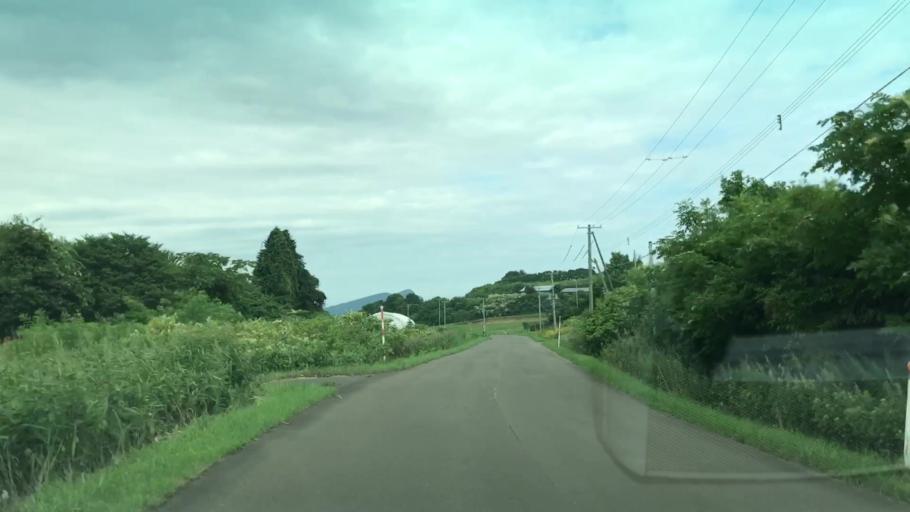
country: JP
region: Hokkaido
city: Yoichi
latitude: 43.1746
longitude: 140.8270
